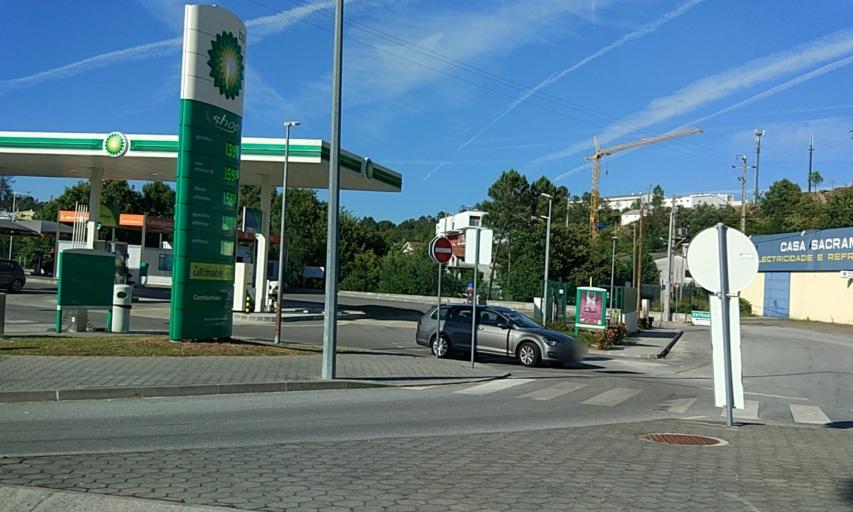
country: PT
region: Viseu
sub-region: Viseu
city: Abraveses
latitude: 40.6820
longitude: -7.9263
